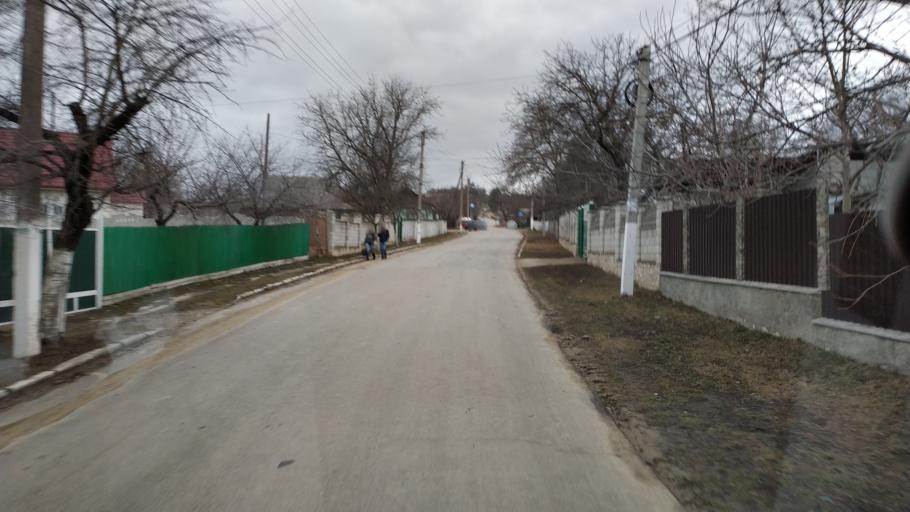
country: MD
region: Calarasi
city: Calarasi
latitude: 47.2632
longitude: 28.1330
